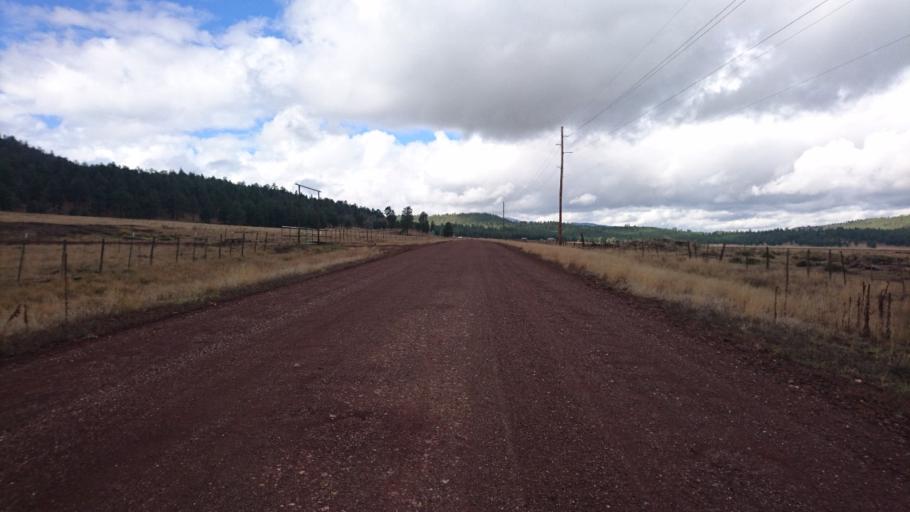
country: US
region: Arizona
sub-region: Coconino County
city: Parks
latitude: 35.2674
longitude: -111.8823
